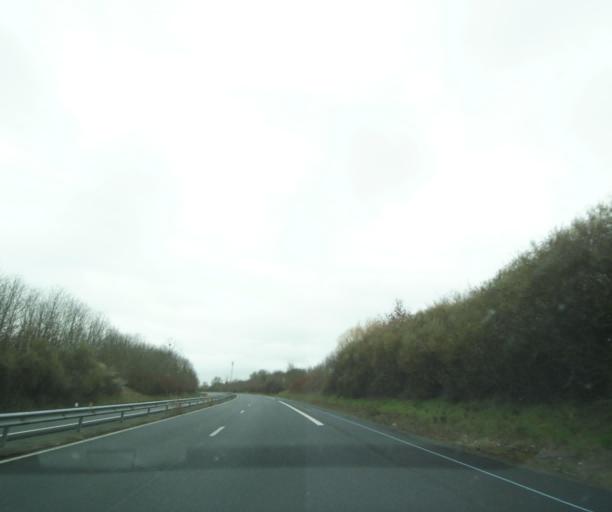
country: FR
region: Poitou-Charentes
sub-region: Departement de la Charente-Maritime
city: Cabariot
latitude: 45.9576
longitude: -0.8622
